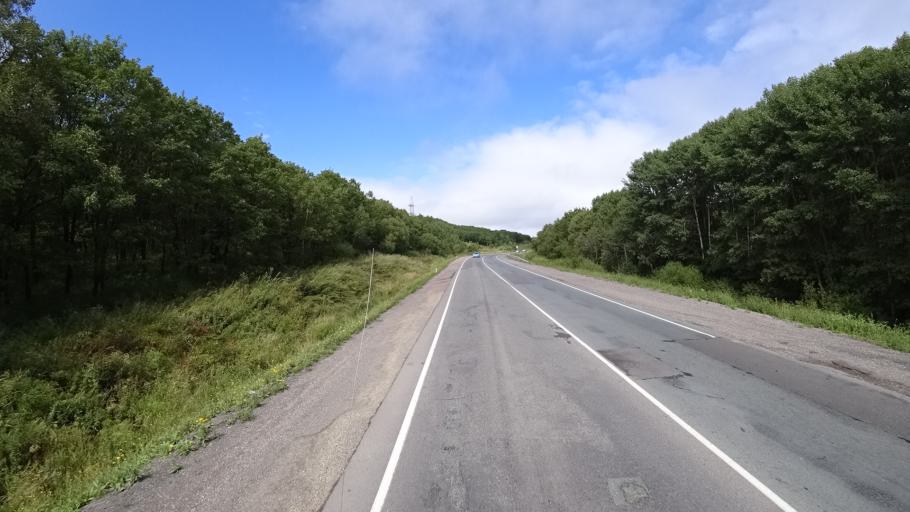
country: RU
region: Primorskiy
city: Lyalichi
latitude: 44.1192
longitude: 132.4196
